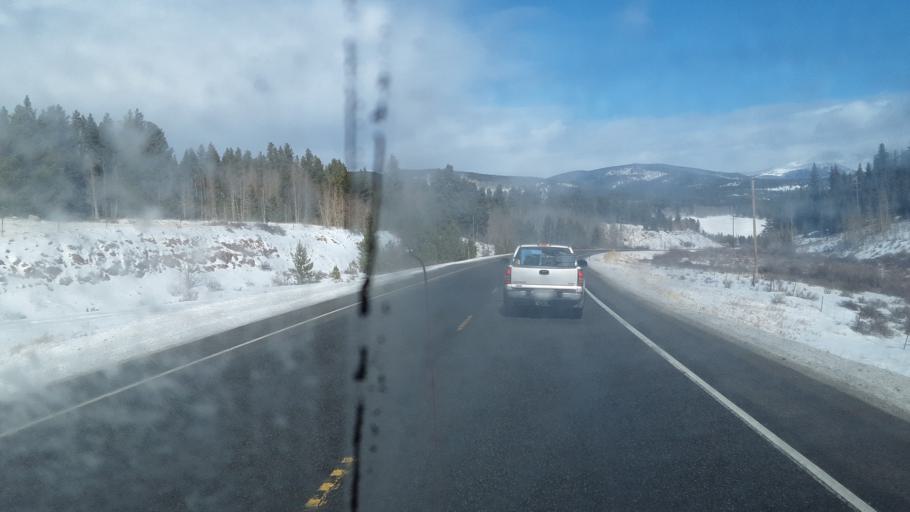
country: US
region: Colorado
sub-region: Summit County
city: Breckenridge
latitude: 39.4254
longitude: -105.7650
